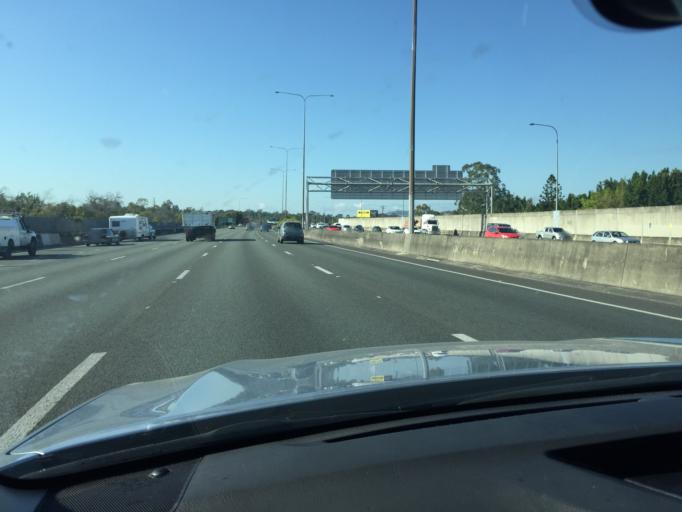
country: AU
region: Queensland
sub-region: Logan
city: Beenleigh
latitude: -27.6926
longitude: 153.1934
